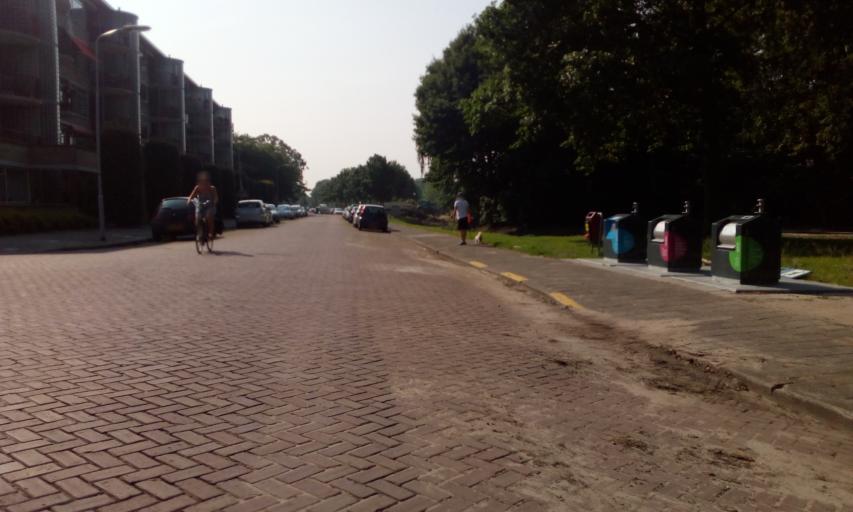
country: NL
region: South Holland
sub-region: Gemeente Leidschendam-Voorburg
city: Voorburg
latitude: 52.0785
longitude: 4.3611
